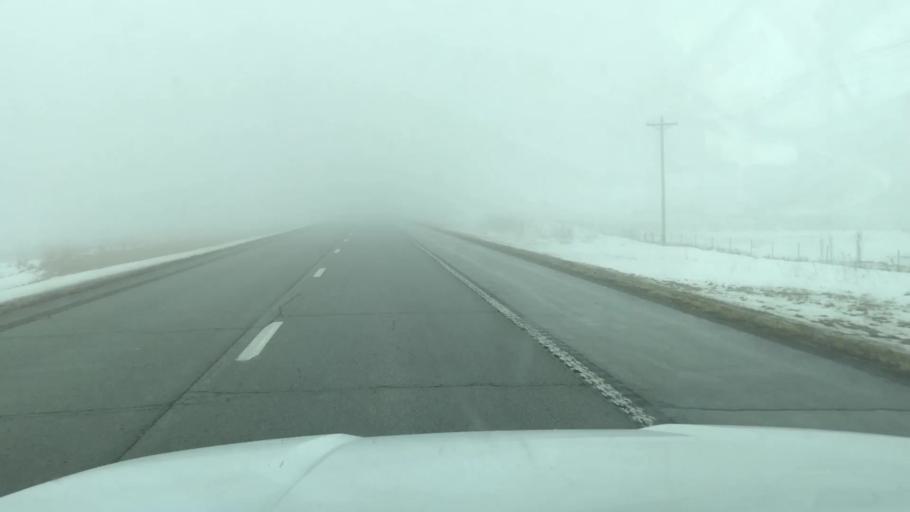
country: US
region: Missouri
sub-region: Clinton County
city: Cameron
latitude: 39.7550
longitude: -94.3047
